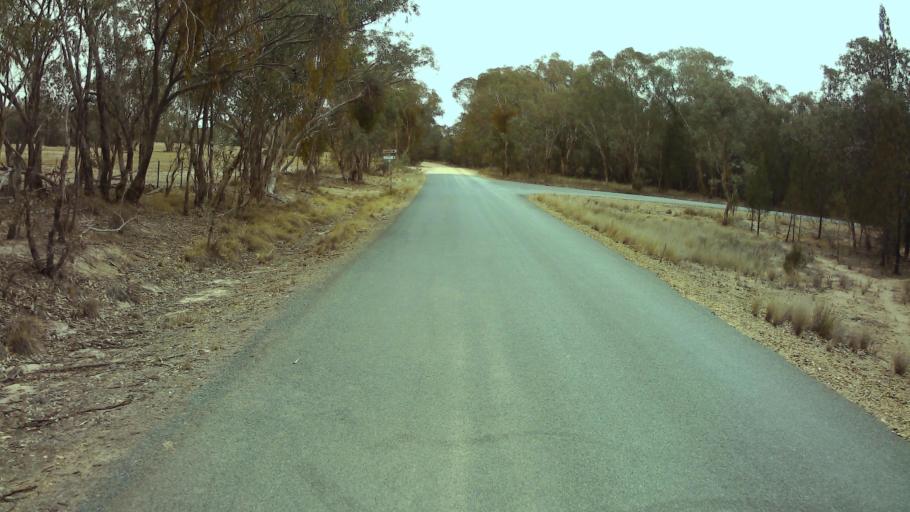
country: AU
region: New South Wales
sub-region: Weddin
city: Grenfell
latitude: -33.8837
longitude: 148.1507
